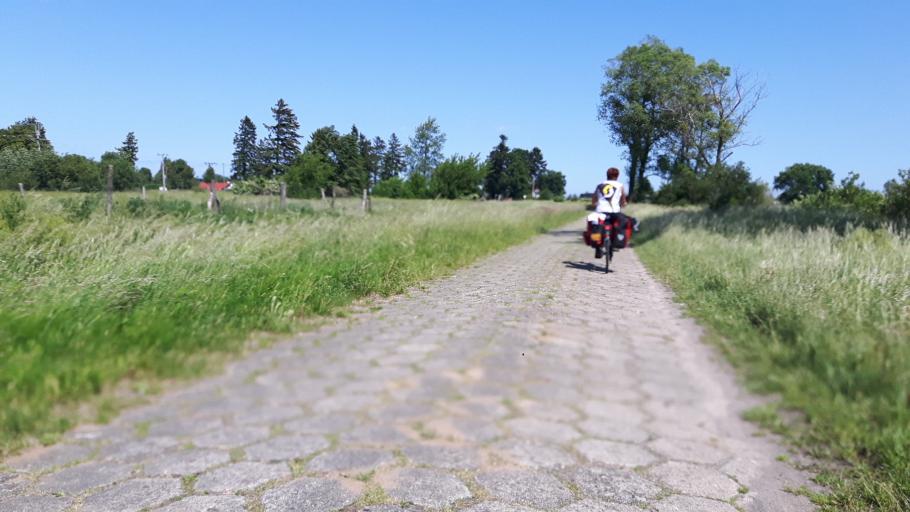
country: PL
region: Pomeranian Voivodeship
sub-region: Powiat slupski
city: Smoldzino
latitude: 54.6853
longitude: 17.2811
